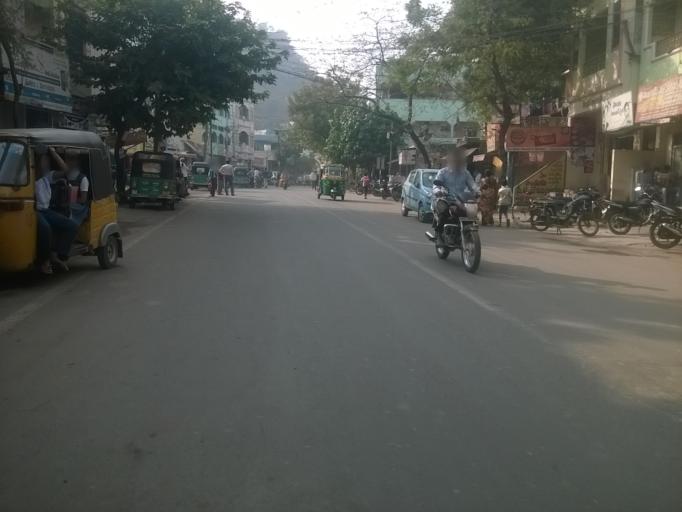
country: IN
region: Andhra Pradesh
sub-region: Krishna
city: Vijayawada
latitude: 16.5247
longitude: 80.6042
